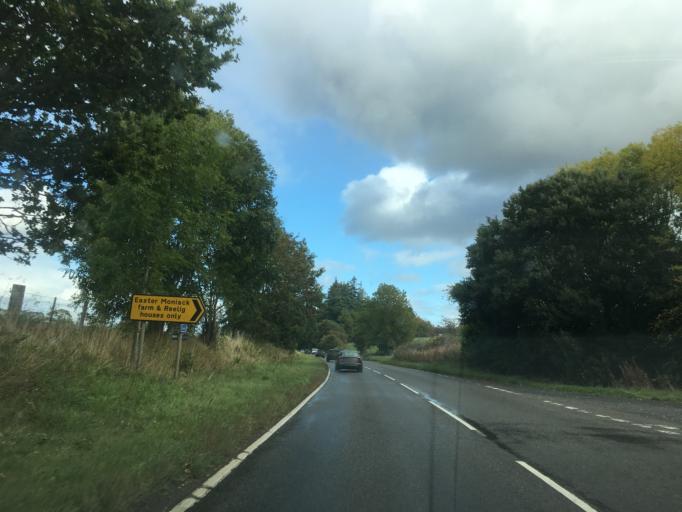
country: GB
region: Scotland
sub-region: Highland
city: Beauly
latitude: 57.4660
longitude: -4.4072
